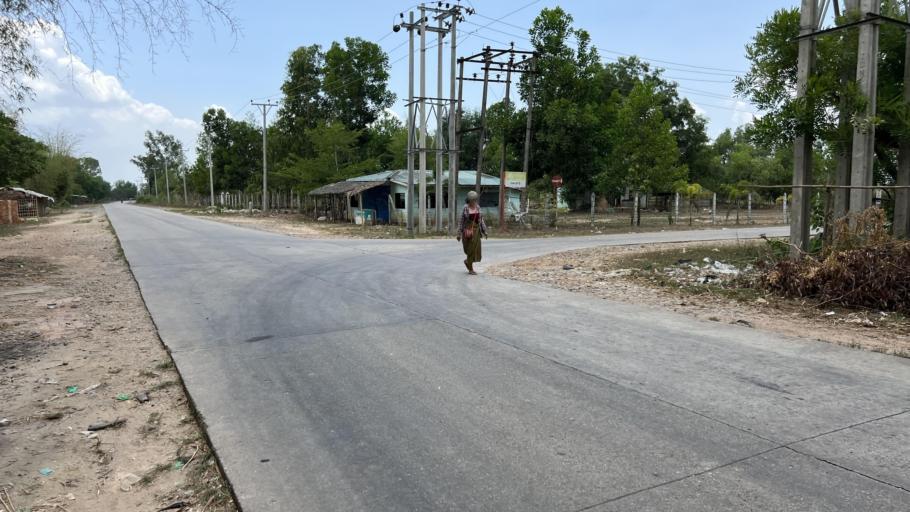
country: MM
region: Yangon
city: Twante
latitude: 16.5337
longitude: 95.9130
